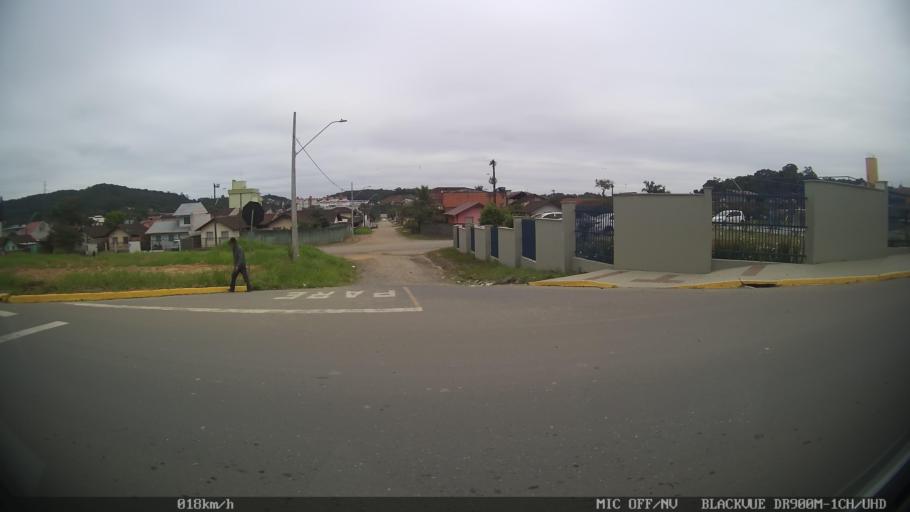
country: BR
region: Santa Catarina
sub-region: Joinville
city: Joinville
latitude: -26.3611
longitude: -48.8079
